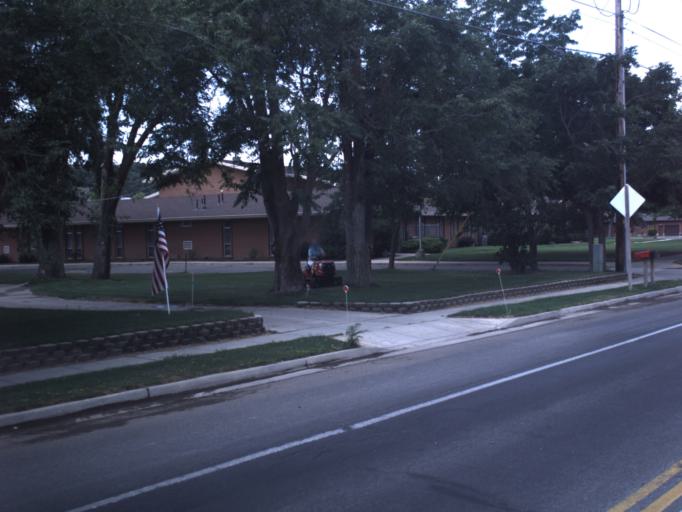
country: US
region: Utah
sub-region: Davis County
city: South Weber
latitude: 41.1340
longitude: -111.9425
